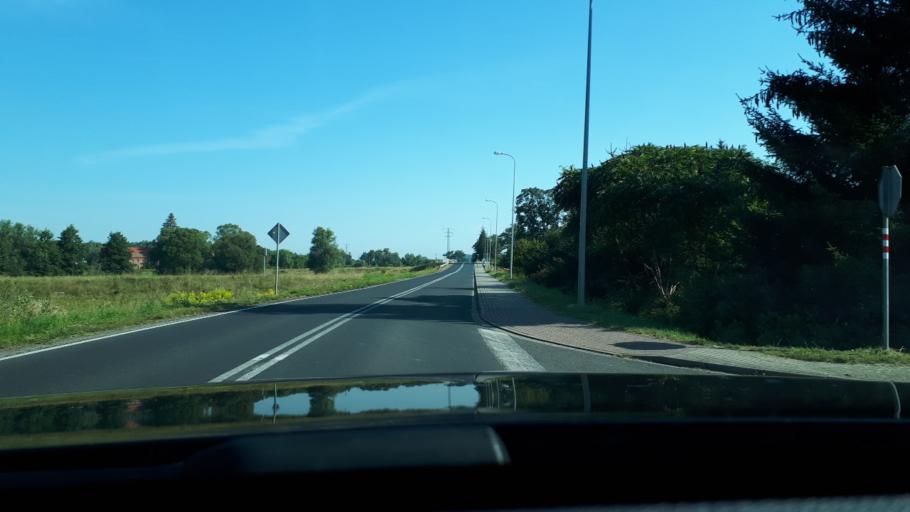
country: PL
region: Lower Silesian Voivodeship
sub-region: Powiat lubanski
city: Luban
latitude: 51.0805
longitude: 15.2950
